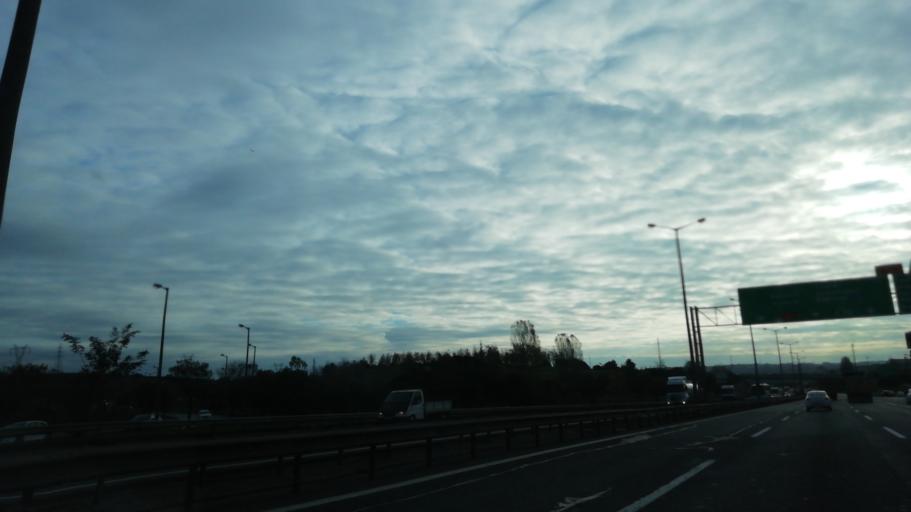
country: TR
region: Istanbul
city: Sultanbeyli
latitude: 40.9383
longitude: 29.3284
